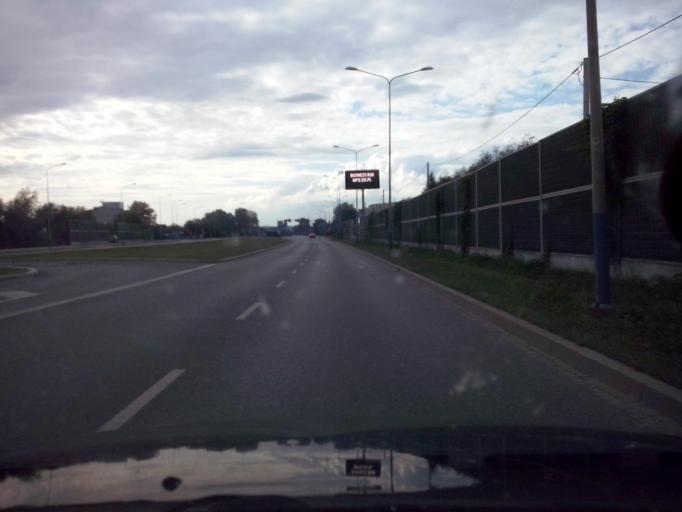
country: PL
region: Lesser Poland Voivodeship
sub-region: Powiat wielicki
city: Czarnochowice
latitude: 50.0390
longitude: 20.0085
